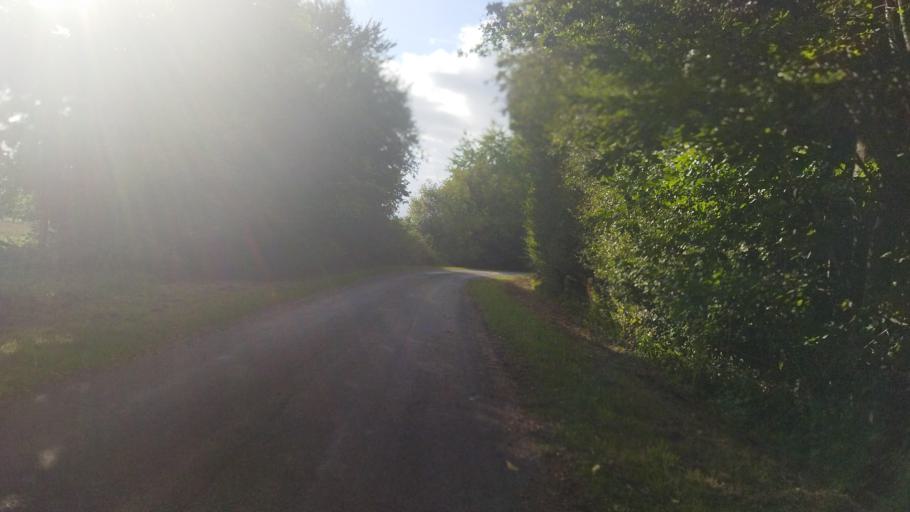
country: DE
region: North Rhine-Westphalia
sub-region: Regierungsbezirk Munster
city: Dulmen
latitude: 51.8768
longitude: 7.2620
